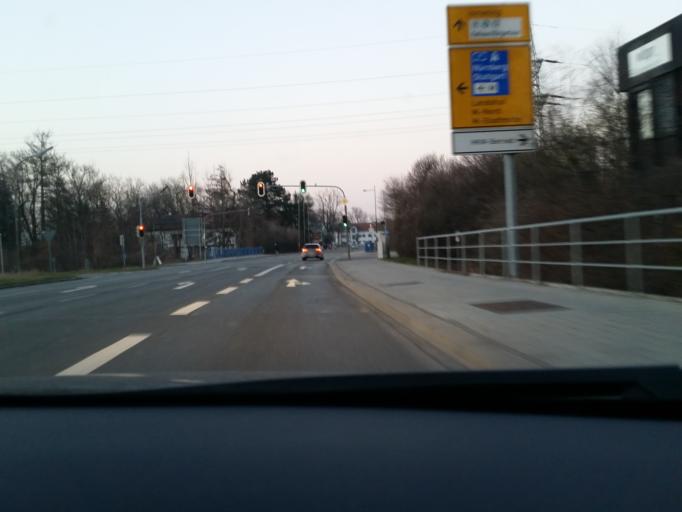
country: DE
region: Bavaria
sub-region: Upper Bavaria
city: Unterfoehring
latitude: 48.1822
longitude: 11.6325
